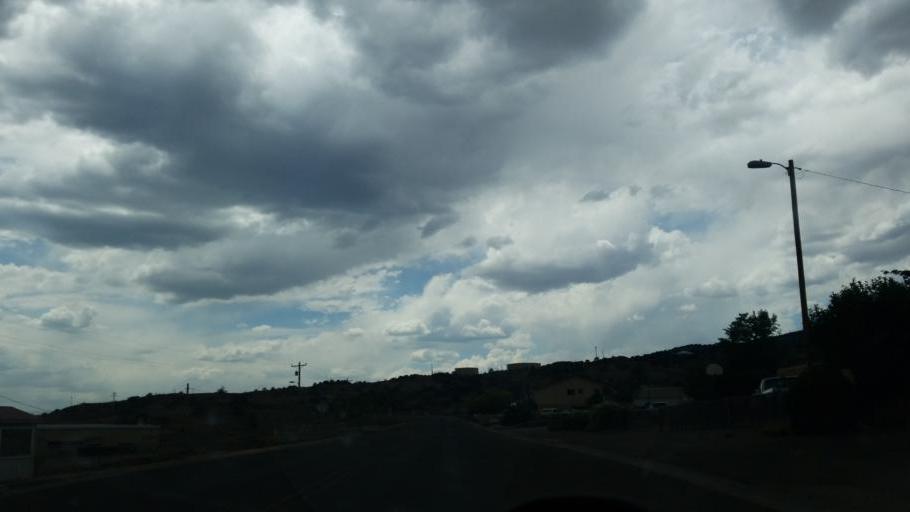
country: US
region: New Mexico
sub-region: Cibola County
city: Grants
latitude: 35.1612
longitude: -107.8457
